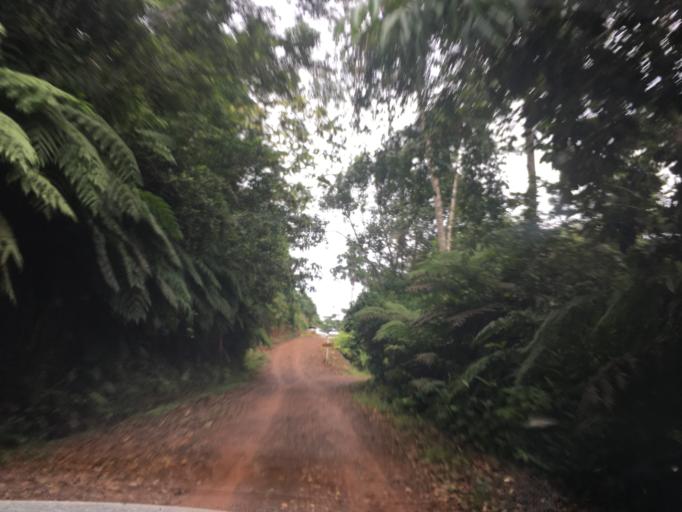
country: BZ
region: Stann Creek
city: Placencia
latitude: 16.7454
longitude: -88.4480
